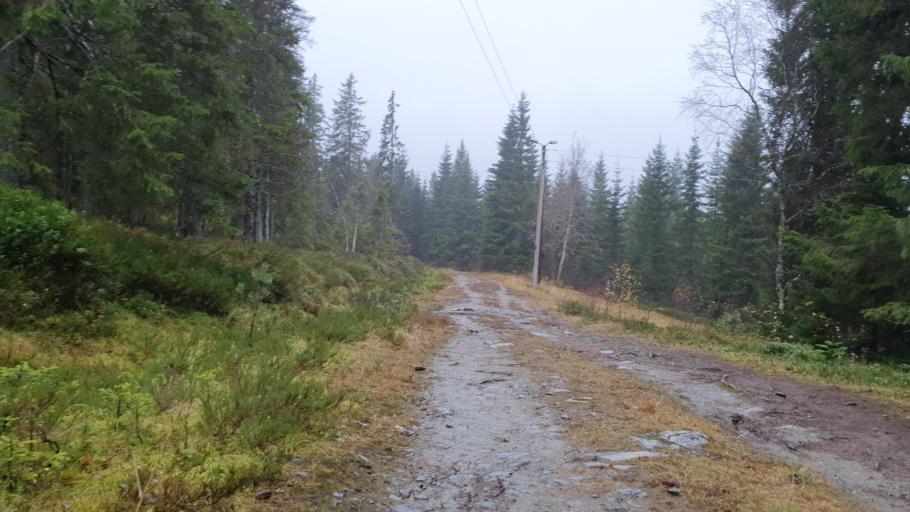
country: NO
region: Sor-Trondelag
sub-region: Trondheim
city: Trondheim
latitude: 63.4140
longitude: 10.3131
